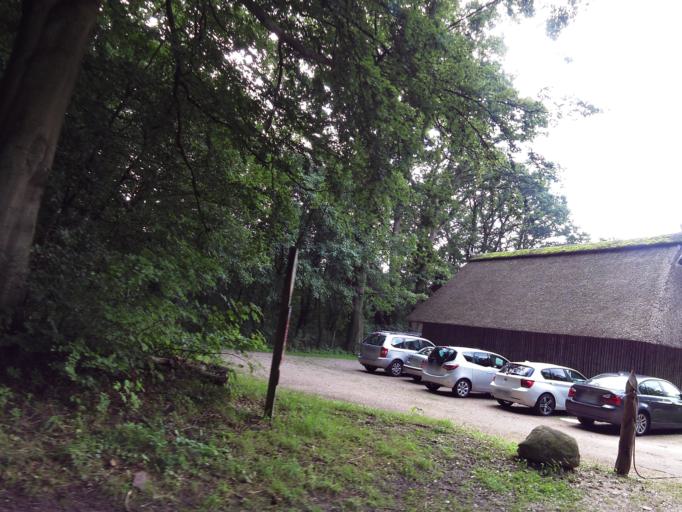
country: DE
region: Lower Saxony
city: Undeloh
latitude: 53.1493
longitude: 9.9101
